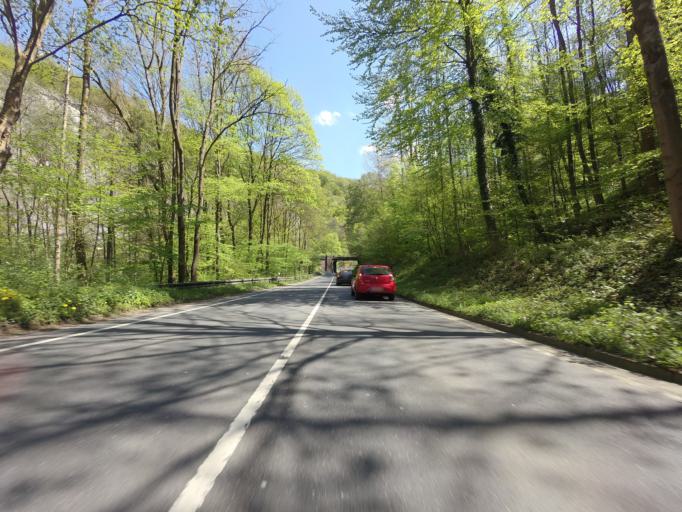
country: DE
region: North Rhine-Westphalia
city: Balve
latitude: 51.3858
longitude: 7.8493
